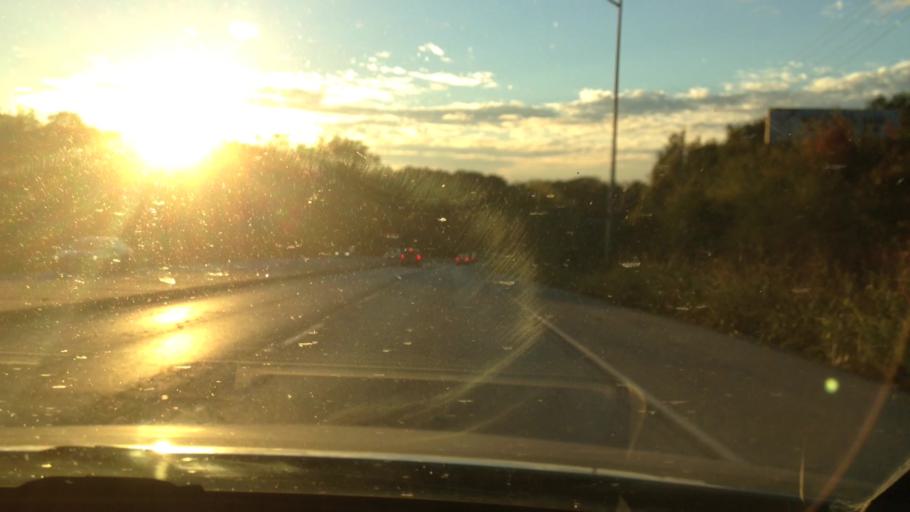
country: US
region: Missouri
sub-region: Jackson County
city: Raytown
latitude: 39.0101
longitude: -94.4928
